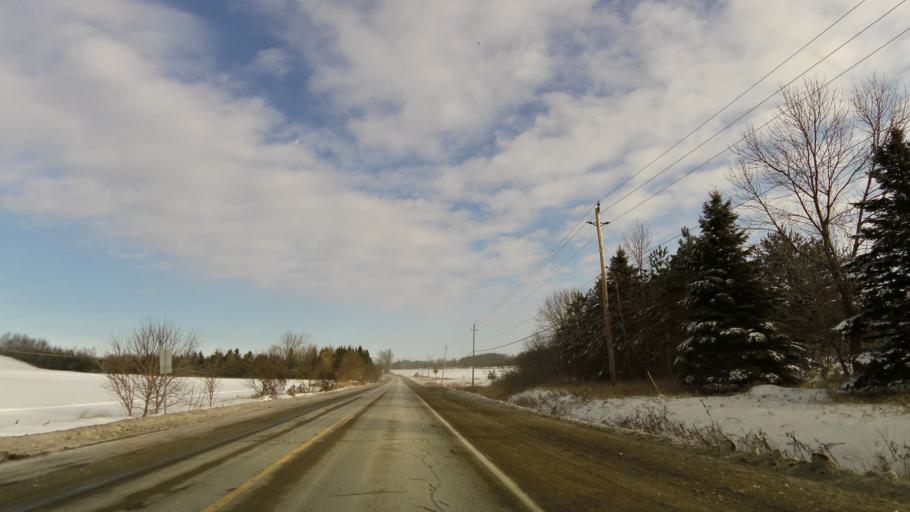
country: CA
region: Ontario
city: Quinte West
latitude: 44.0919
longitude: -77.7720
